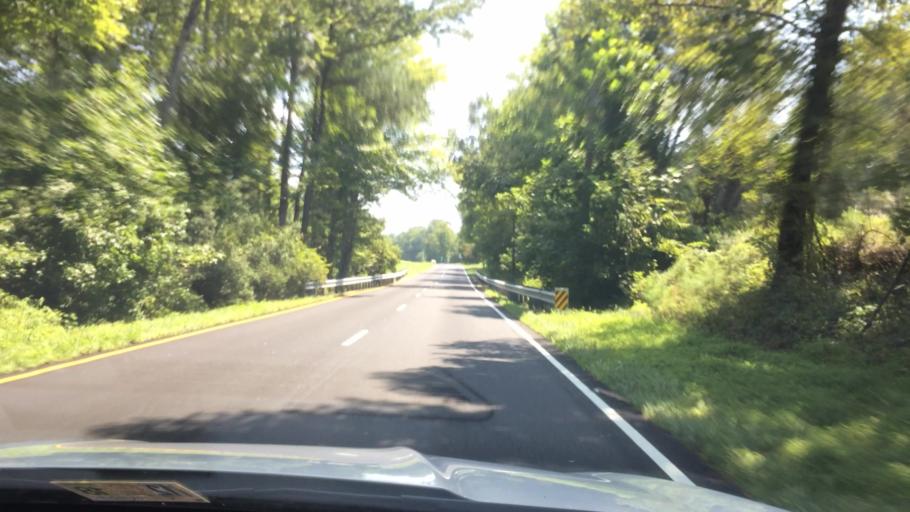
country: US
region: Virginia
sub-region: Charles City County
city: Charles City
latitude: 37.4442
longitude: -77.0542
